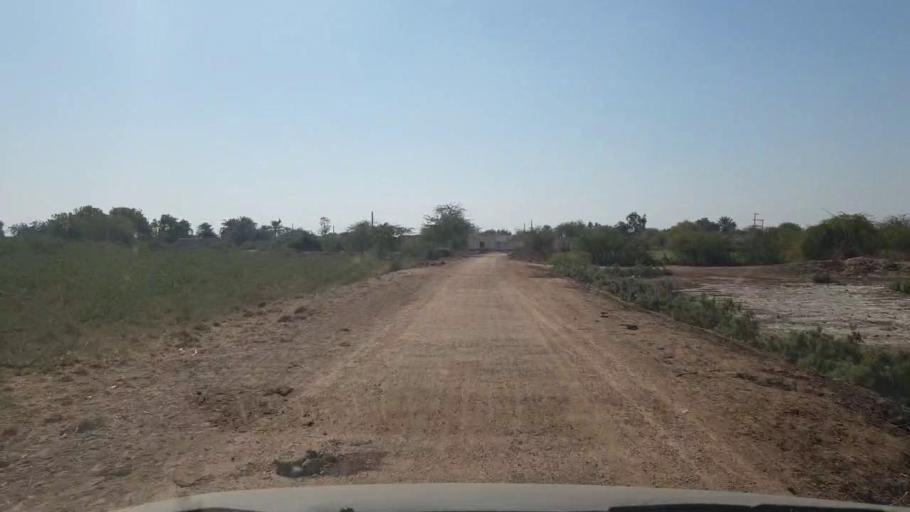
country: PK
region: Sindh
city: Mirwah Gorchani
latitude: 25.2900
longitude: 69.1206
